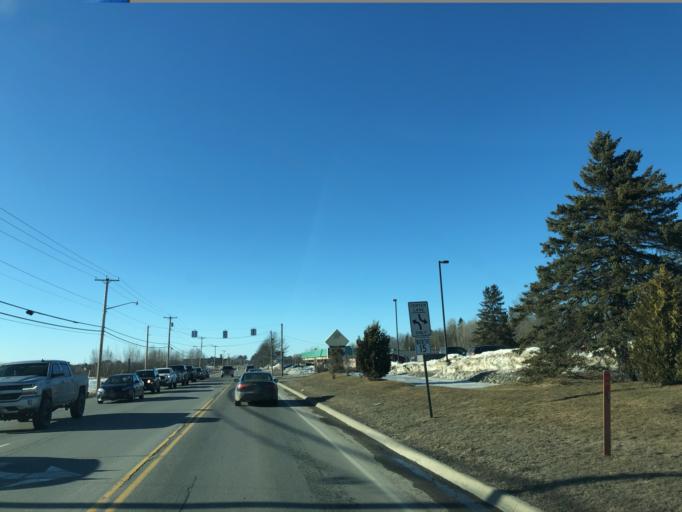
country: US
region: Maine
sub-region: Penobscot County
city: Bangor
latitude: 44.8367
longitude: -68.7919
